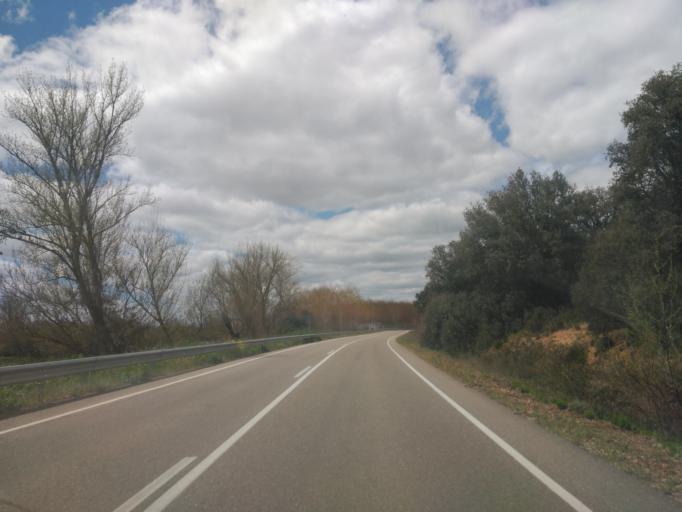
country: ES
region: Castille and Leon
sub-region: Provincia de Salamanca
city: Florida de Liebana
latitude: 41.0395
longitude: -5.7506
